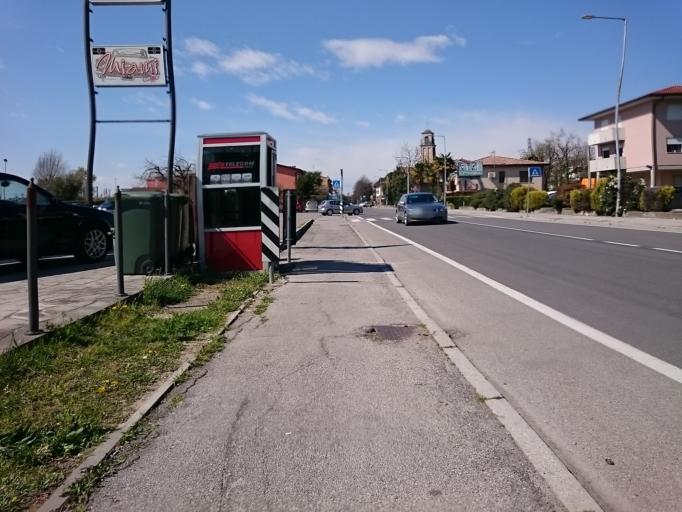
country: IT
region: Veneto
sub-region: Provincia di Padova
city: Brugine
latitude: 45.2962
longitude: 11.9951
